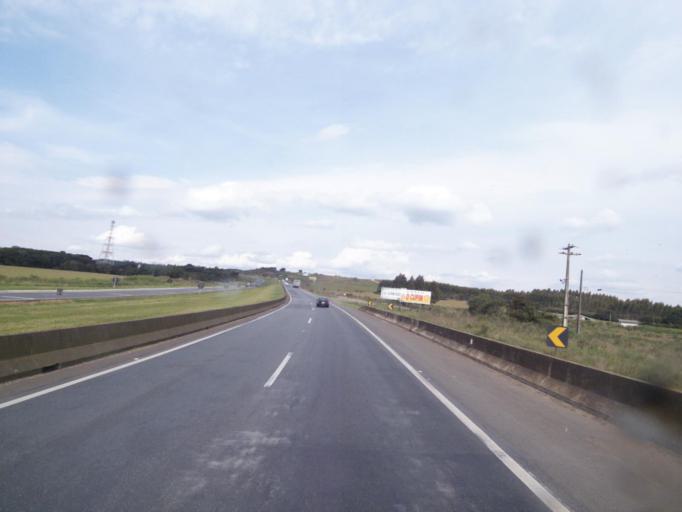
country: BR
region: Parana
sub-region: Campo Largo
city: Campo Largo
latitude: -25.4759
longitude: -49.7194
